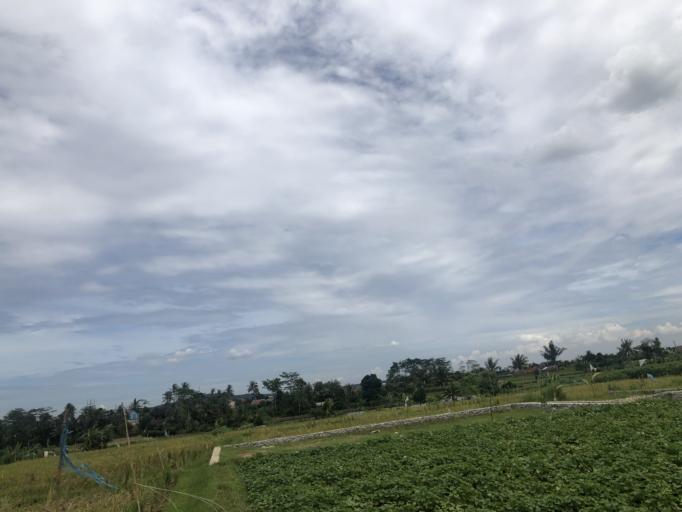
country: ID
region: West Java
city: Ciampea
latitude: -6.5495
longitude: 106.7393
